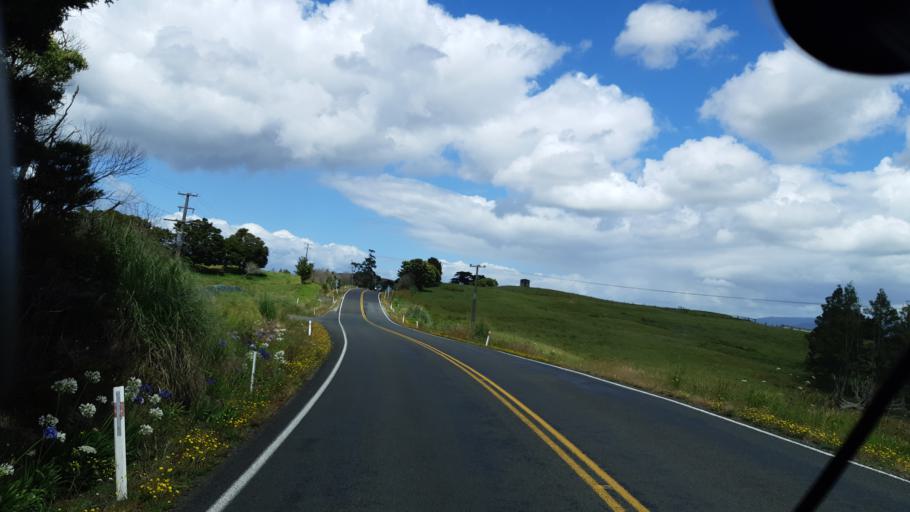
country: NZ
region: Northland
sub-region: Far North District
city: Waimate North
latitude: -35.3011
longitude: 173.5979
